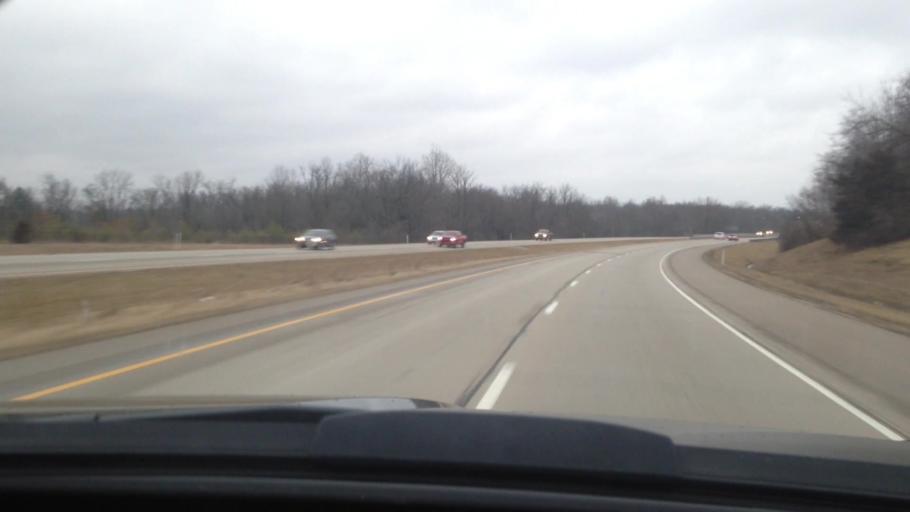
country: US
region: Indiana
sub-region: Delaware County
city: Muncie
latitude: 40.1751
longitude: -85.3381
